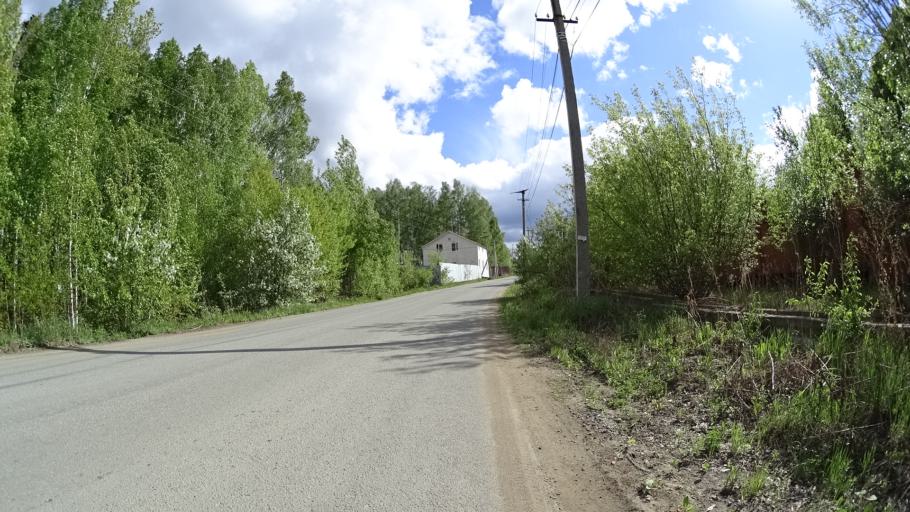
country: RU
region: Chelyabinsk
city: Sargazy
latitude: 55.1511
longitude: 61.2382
